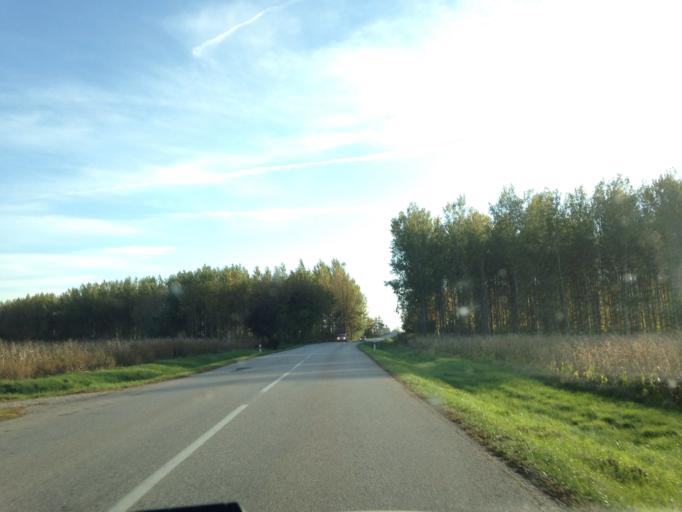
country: SK
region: Nitriansky
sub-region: Okres Komarno
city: Hurbanovo
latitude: 47.8280
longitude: 18.2351
